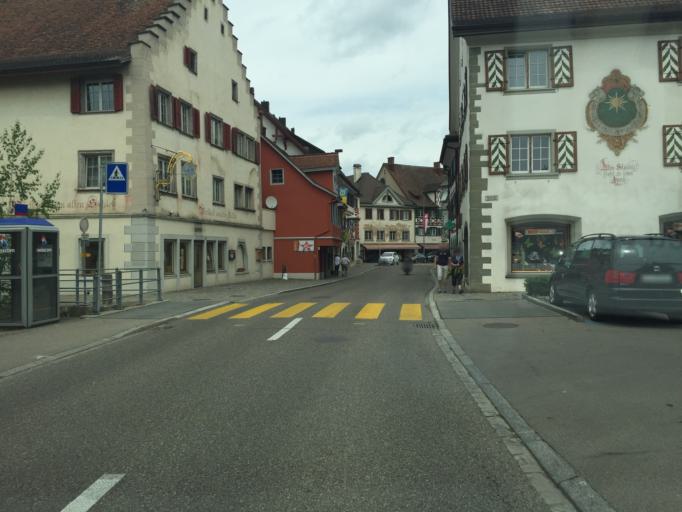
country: CH
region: Thurgau
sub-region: Frauenfeld District
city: Steckborn
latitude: 47.6668
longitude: 8.9814
